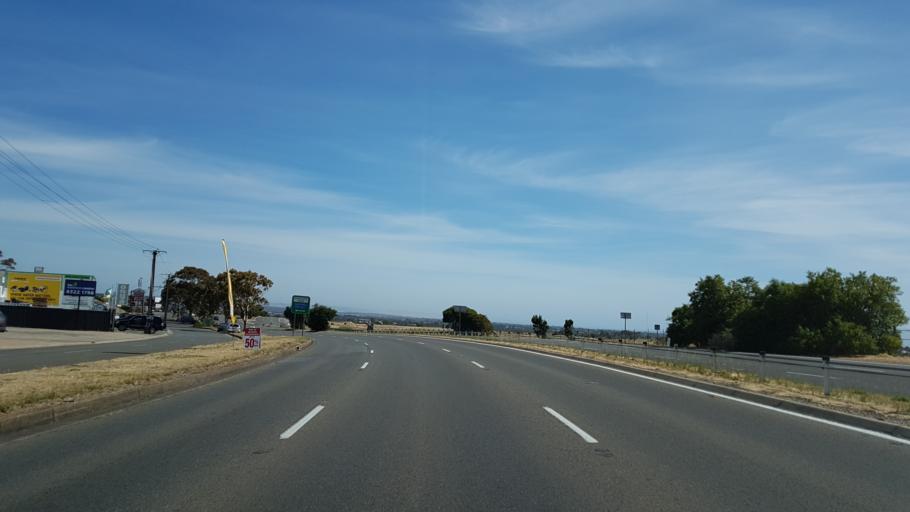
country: AU
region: South Australia
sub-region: Marion
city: Trott Park
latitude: -35.0643
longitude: 138.5552
